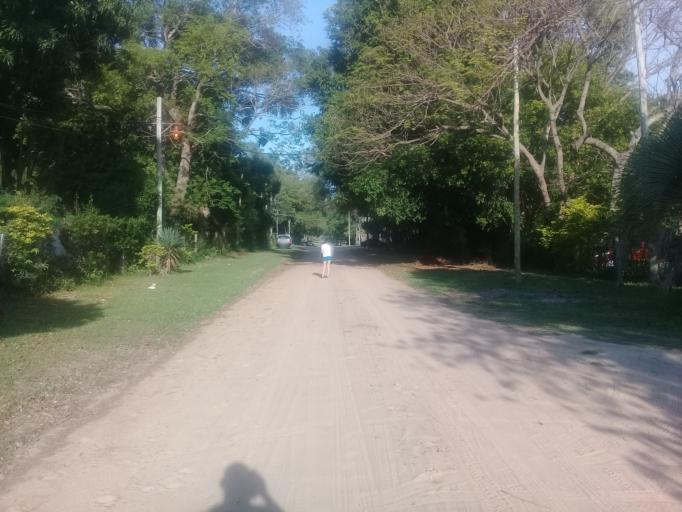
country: AR
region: Corrientes
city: San Luis del Palmar
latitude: -27.4534
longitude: -58.6561
